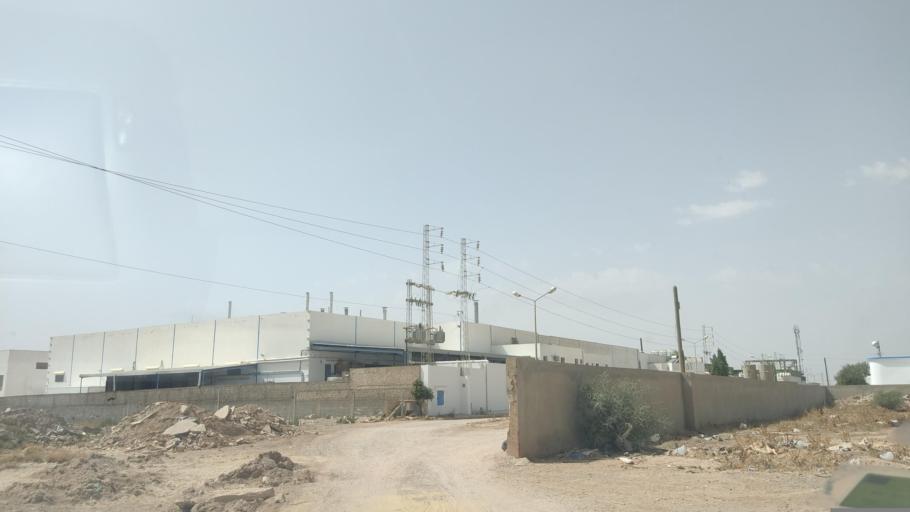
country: TN
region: Tunis
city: La Mohammedia
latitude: 36.5598
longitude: 10.0816
